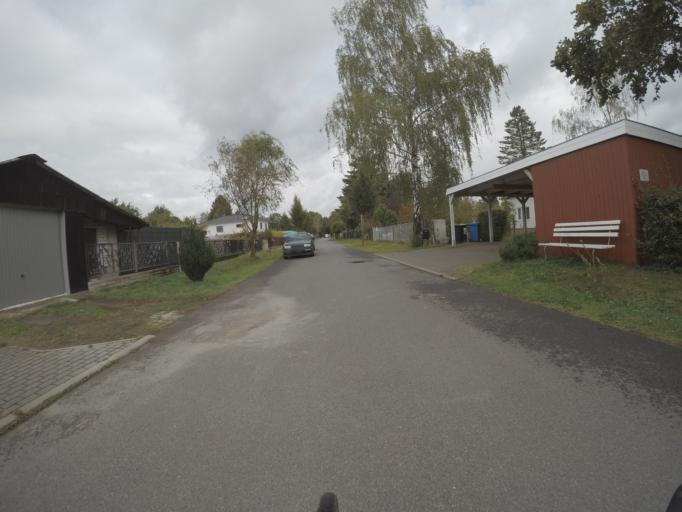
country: DE
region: Berlin
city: Buch
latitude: 52.6798
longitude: 13.4691
